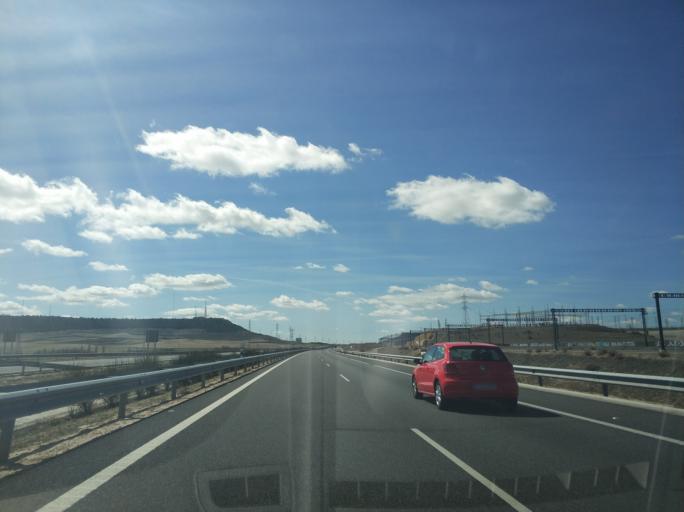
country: ES
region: Castille and Leon
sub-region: Provincia de Valladolid
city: Cisterniga
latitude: 41.6478
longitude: -4.6725
